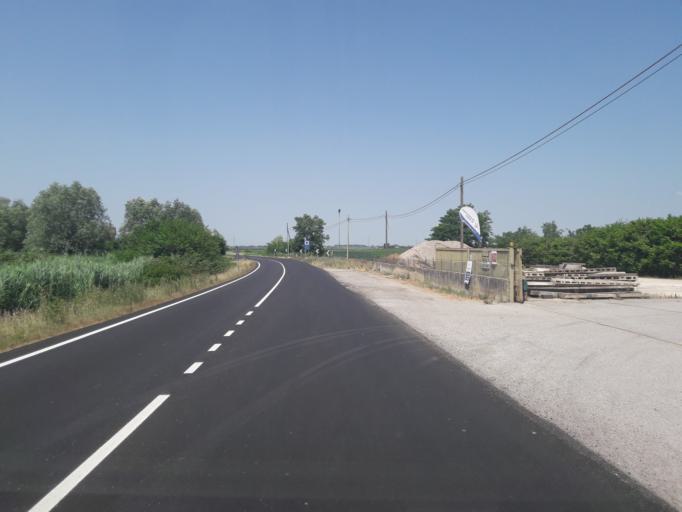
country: IT
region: Veneto
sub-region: Provincia di Rovigo
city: Taglio di Po
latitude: 45.0040
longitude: 12.1989
